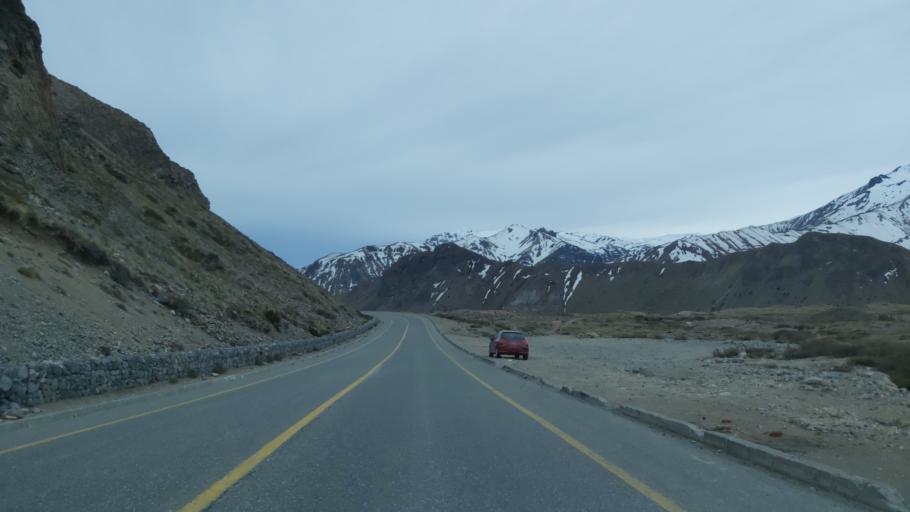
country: CL
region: Maule
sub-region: Provincia de Linares
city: Colbun
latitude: -35.9594
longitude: -70.5728
